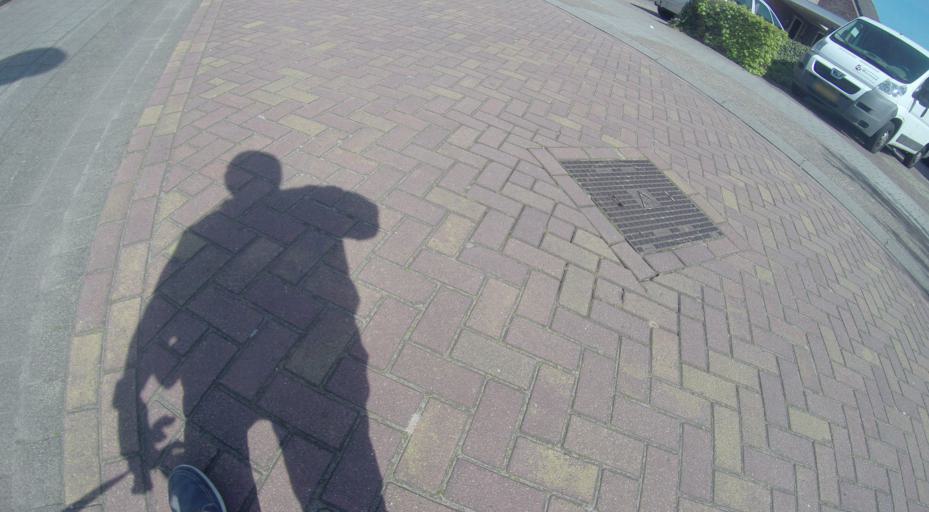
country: NL
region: Gelderland
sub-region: Oost Gelre
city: Lichtenvoorde
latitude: 52.0006
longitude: 6.5187
